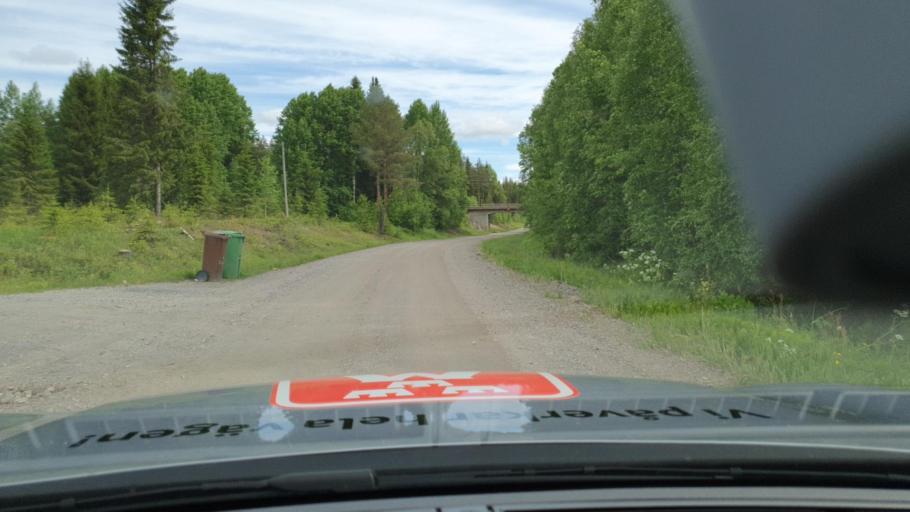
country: SE
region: Norrbotten
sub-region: Kalix Kommun
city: Rolfs
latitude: 65.8859
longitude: 23.0840
